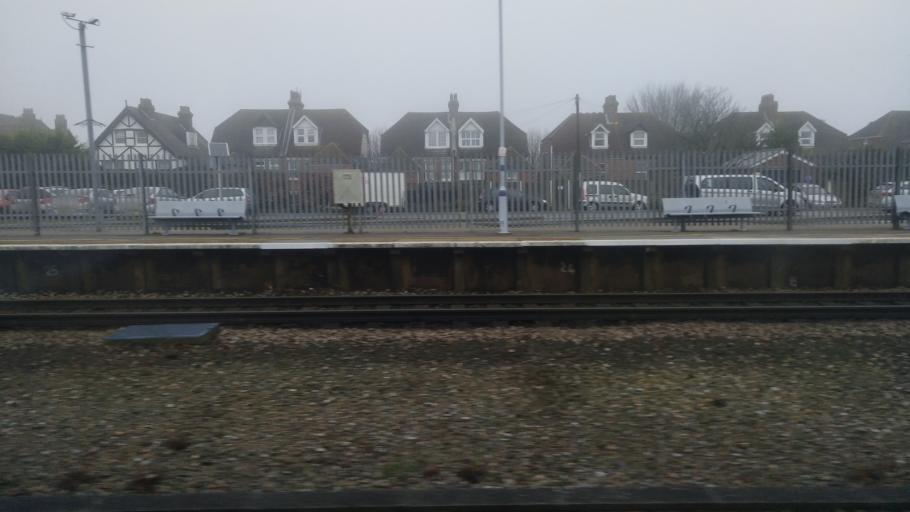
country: GB
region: England
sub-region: Kent
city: Hawkinge
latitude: 51.0848
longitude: 1.1533
